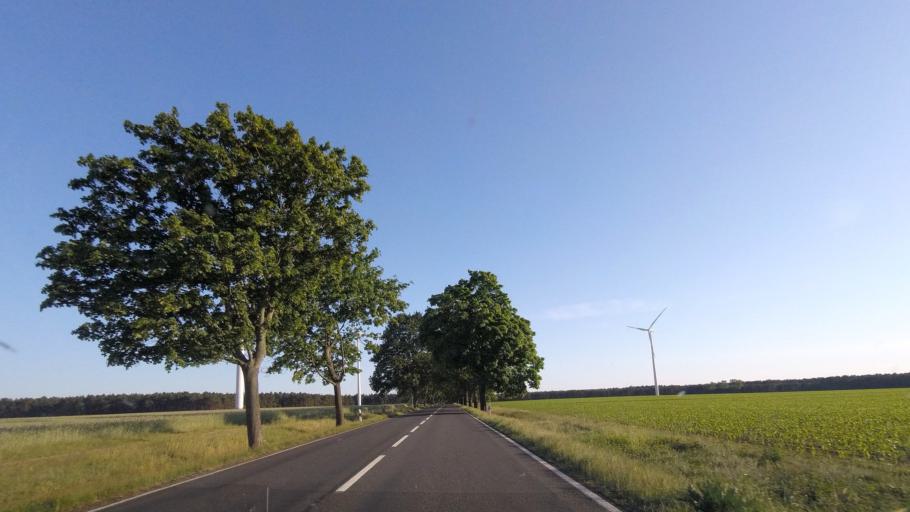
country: DE
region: Brandenburg
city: Golzow
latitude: 52.3104
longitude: 12.6090
